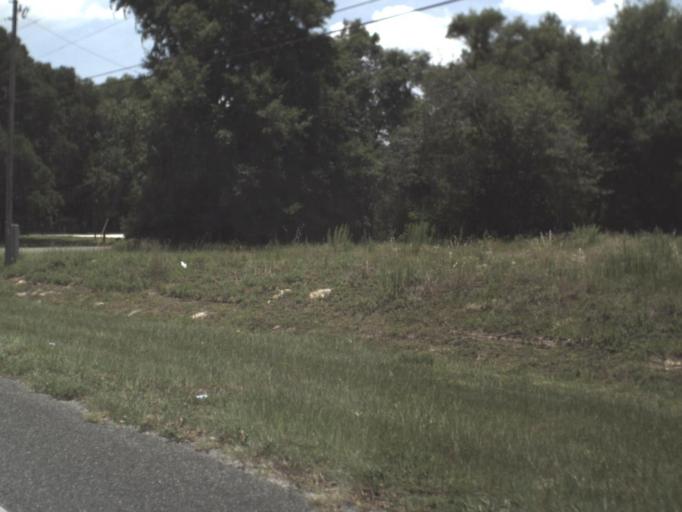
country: US
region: Florida
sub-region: Dixie County
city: Cross City
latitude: 29.6069
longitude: -83.0552
